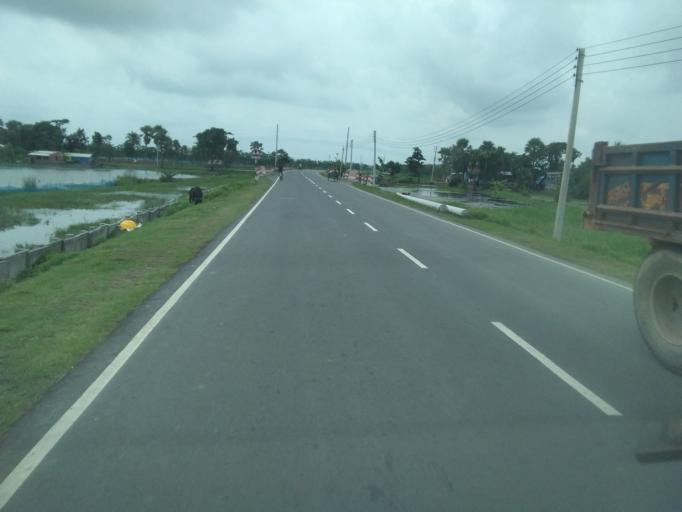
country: BD
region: Khulna
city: Satkhira
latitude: 22.7047
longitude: 89.0555
